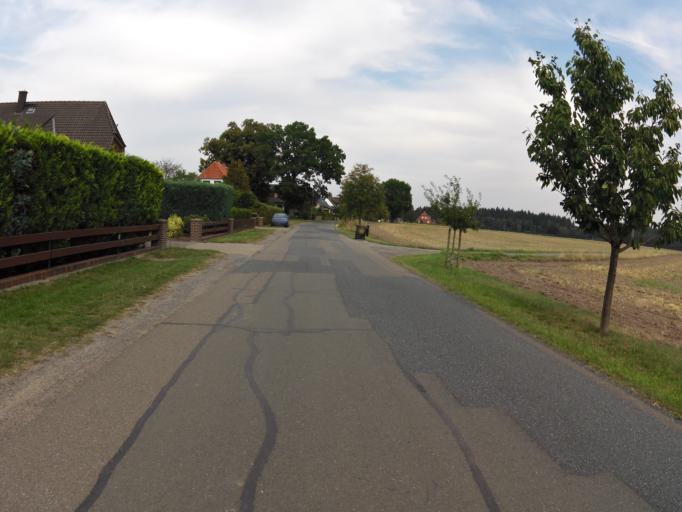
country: DE
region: Lower Saxony
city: Estorf
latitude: 52.5969
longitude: 9.1815
